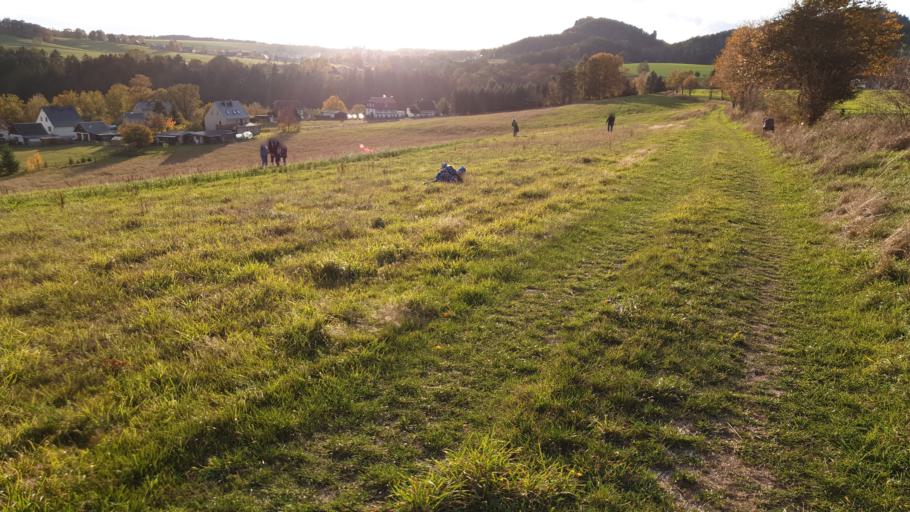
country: DE
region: Saxony
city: Bad Schandau
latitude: 50.9054
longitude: 14.1530
